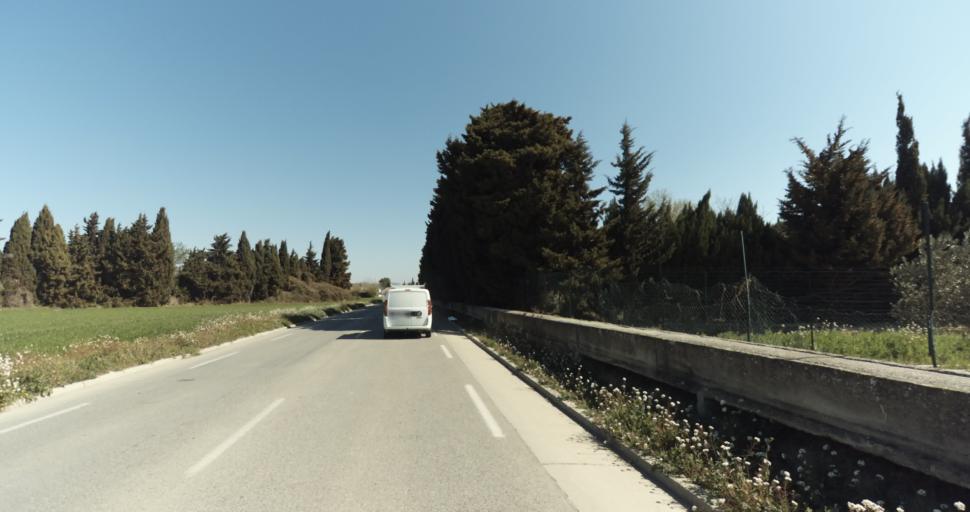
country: FR
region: Provence-Alpes-Cote d'Azur
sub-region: Departement des Bouches-du-Rhone
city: Pelissanne
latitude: 43.6248
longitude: 5.1480
